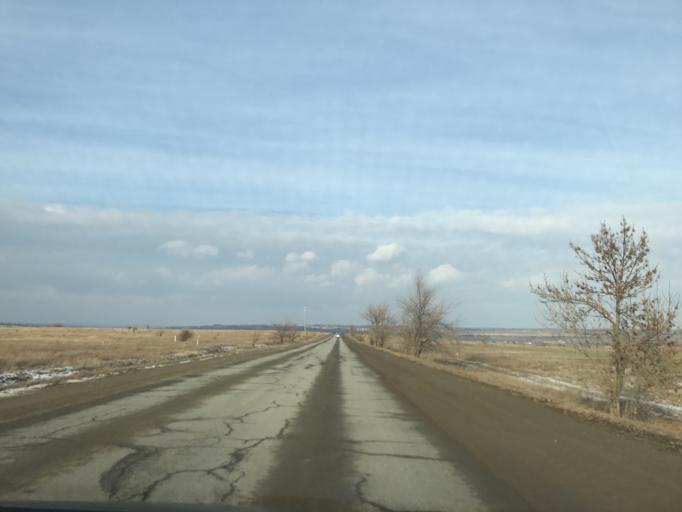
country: RU
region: Rostov
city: Staraya Stanitsa
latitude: 48.2760
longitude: 40.3460
